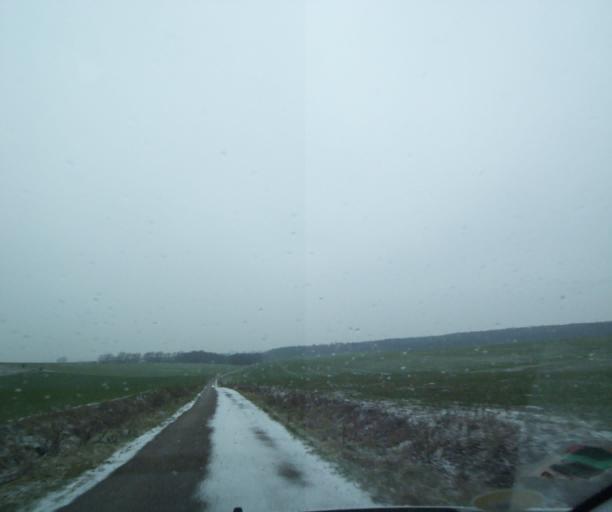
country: FR
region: Champagne-Ardenne
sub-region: Departement de la Haute-Marne
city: Wassy
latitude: 48.4623
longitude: 5.0266
